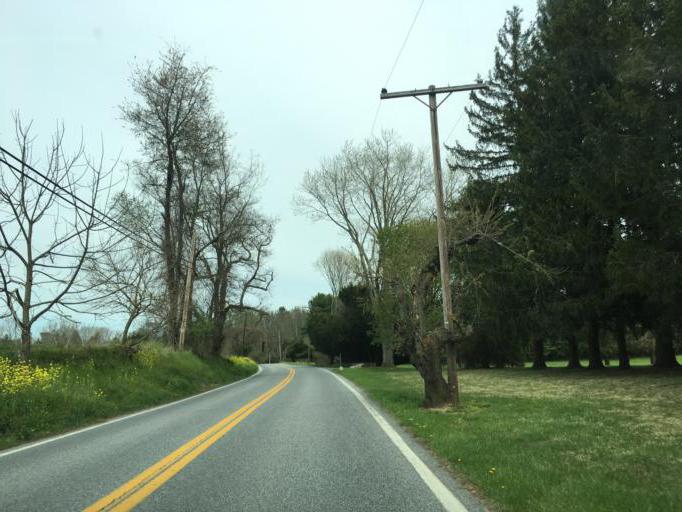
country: US
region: Maryland
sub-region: Baltimore County
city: Hunt Valley
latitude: 39.5499
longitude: -76.6074
